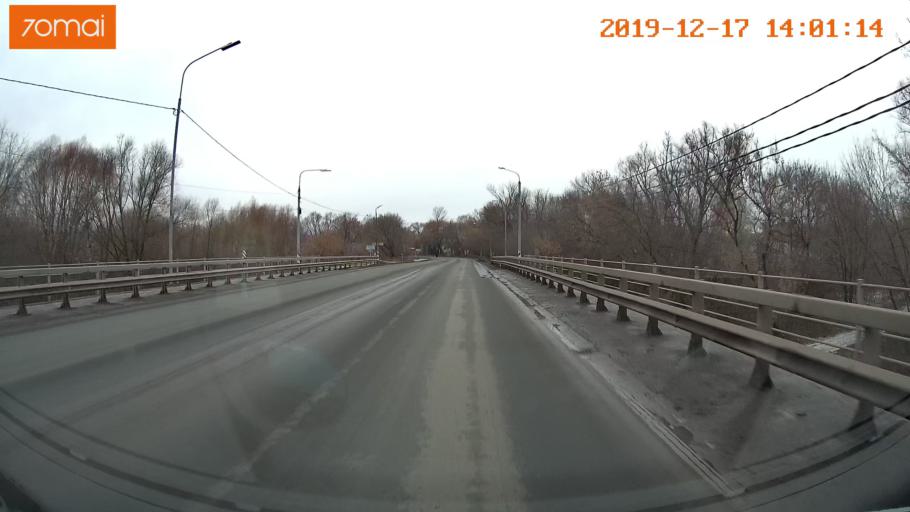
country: RU
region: Rjazan
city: Ryazan'
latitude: 54.6189
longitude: 39.6610
